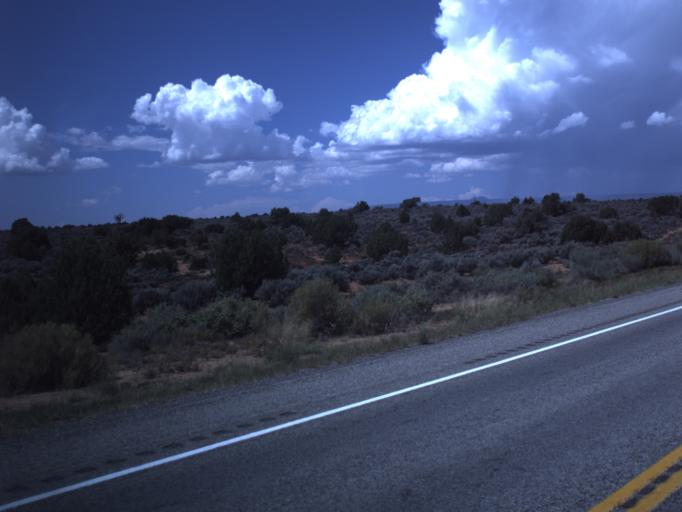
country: US
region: Utah
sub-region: San Juan County
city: Blanding
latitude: 37.4840
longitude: -109.4728
